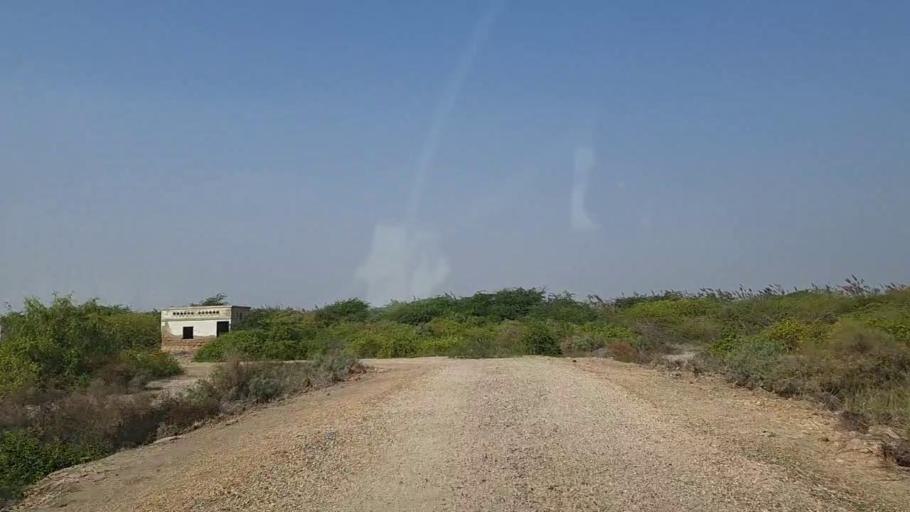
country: PK
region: Sindh
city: Mirpur Sakro
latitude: 24.6611
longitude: 67.7261
